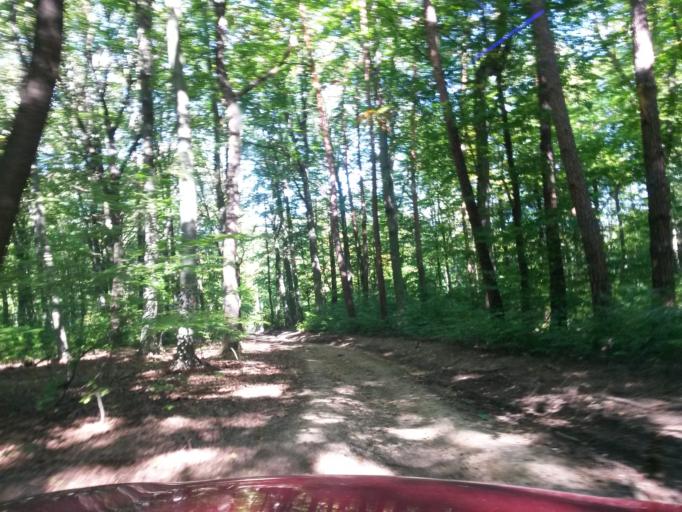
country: SK
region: Presovsky
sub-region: Okres Presov
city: Presov
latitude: 48.9757
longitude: 21.1480
